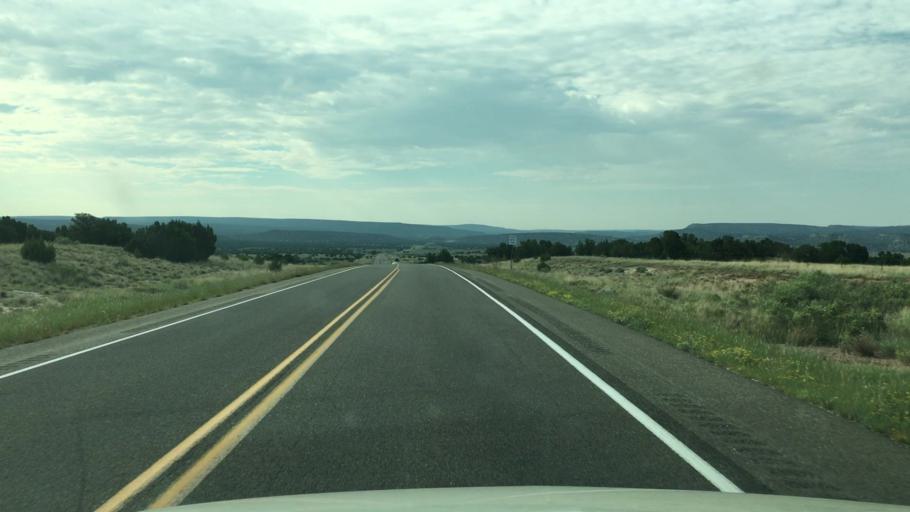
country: US
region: New Mexico
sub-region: Santa Fe County
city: Eldorado at Santa Fe
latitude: 35.4271
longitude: -105.8772
